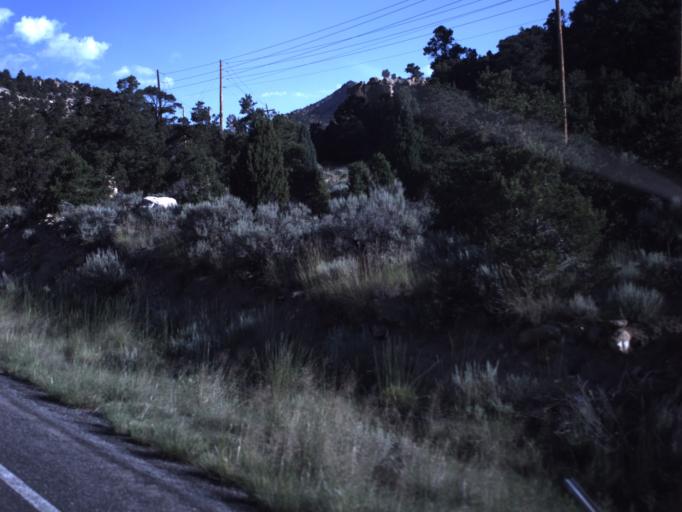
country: US
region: Utah
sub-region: Emery County
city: Huntington
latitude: 39.4058
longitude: -111.1161
